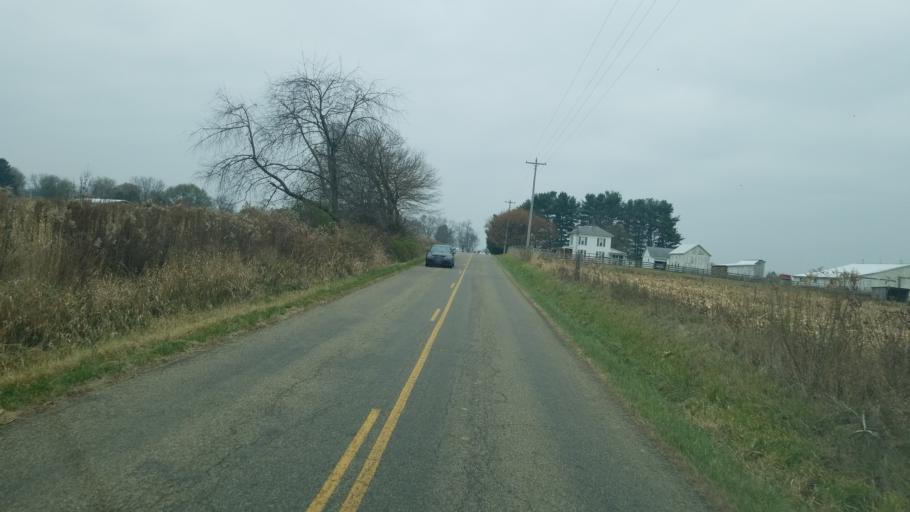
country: US
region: Ohio
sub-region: Knox County
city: Gambier
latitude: 40.3548
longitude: -82.4403
